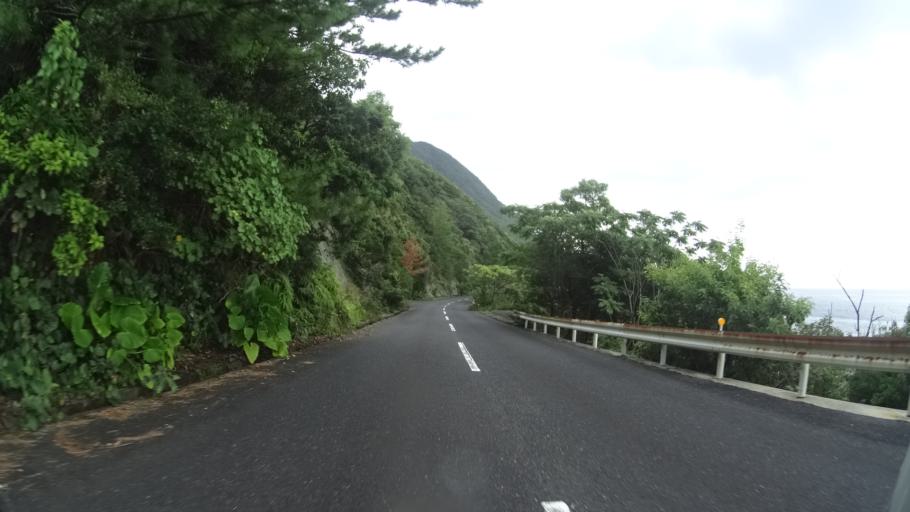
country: JP
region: Kagoshima
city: Nishinoomote
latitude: 30.3162
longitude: 130.4038
